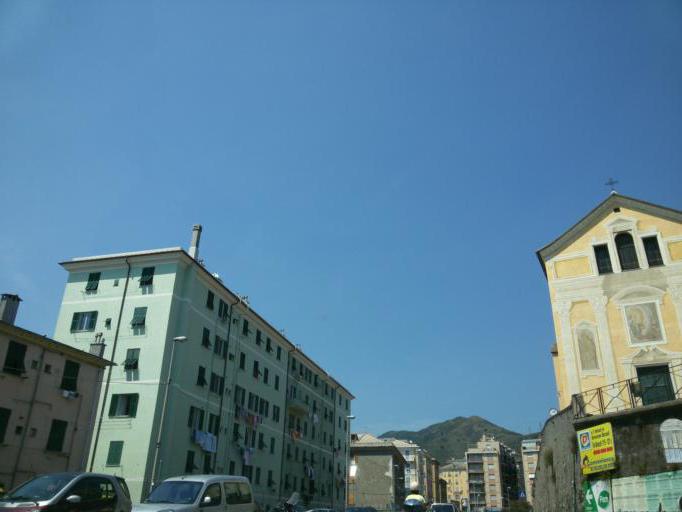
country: IT
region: Liguria
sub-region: Provincia di Genova
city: San Teodoro
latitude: 44.4235
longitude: 8.8547
